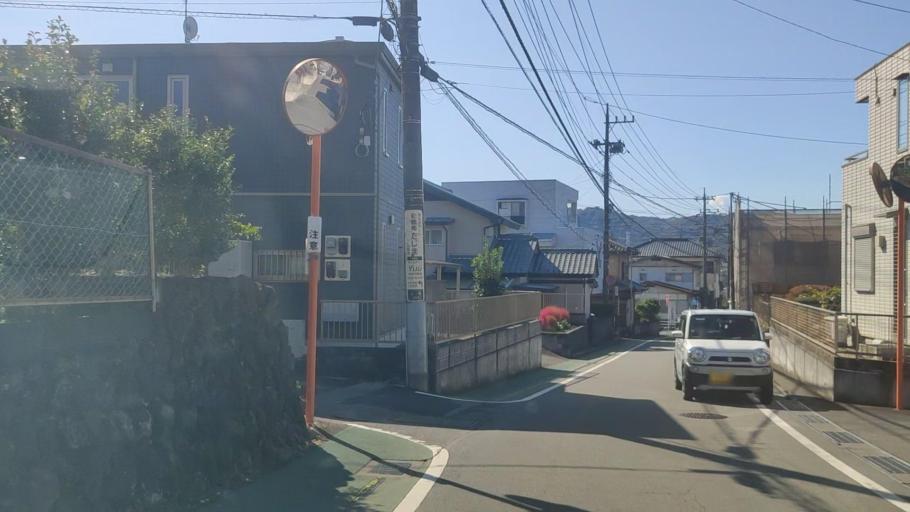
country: JP
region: Shizuoka
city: Mishima
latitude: 35.0040
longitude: 138.9442
